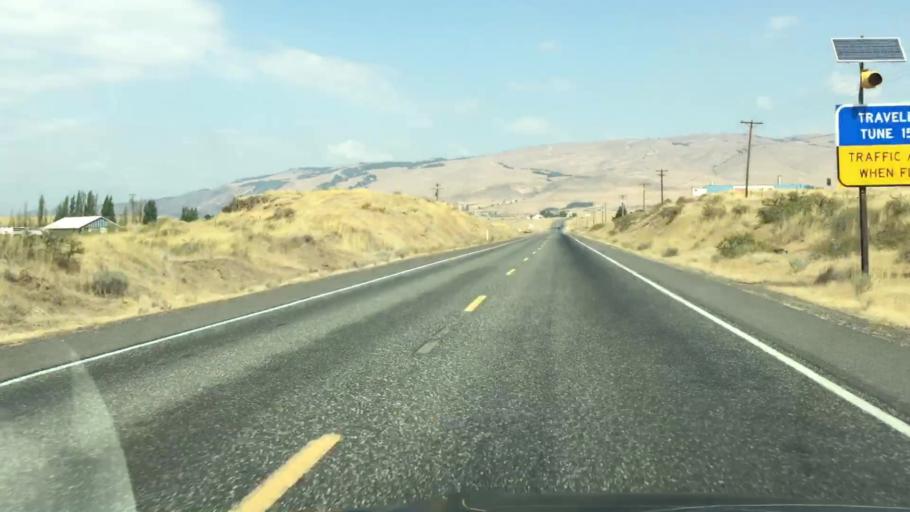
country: US
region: Washington
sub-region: Klickitat County
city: Dallesport
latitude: 45.6246
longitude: -121.1479
